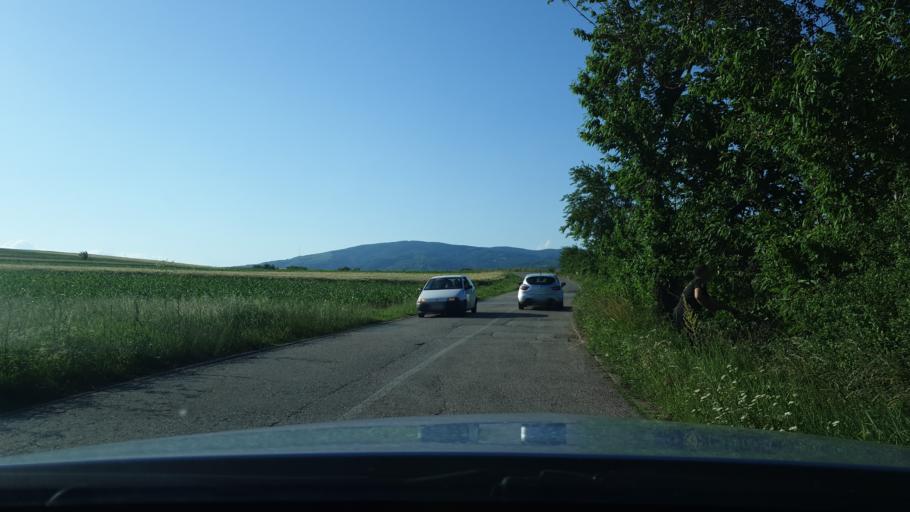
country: RS
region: Central Serbia
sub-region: Nisavski Okrug
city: Aleksinac
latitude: 43.6188
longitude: 21.6802
